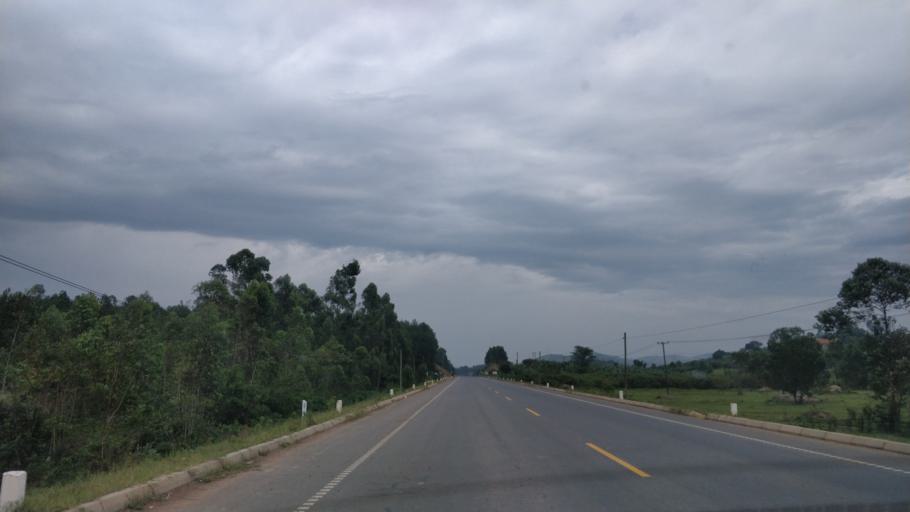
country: UG
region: Western Region
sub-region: Sheema District
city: Kibingo
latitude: -0.6715
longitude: 30.4322
